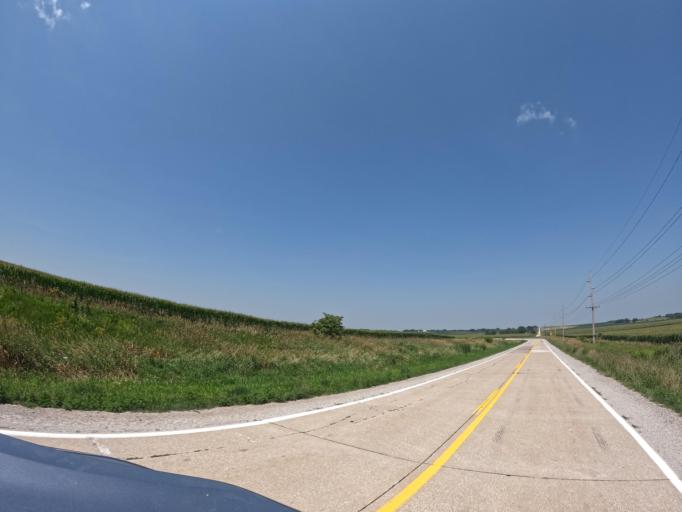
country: US
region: Iowa
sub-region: Keokuk County
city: Sigourney
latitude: 41.2836
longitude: -92.1808
